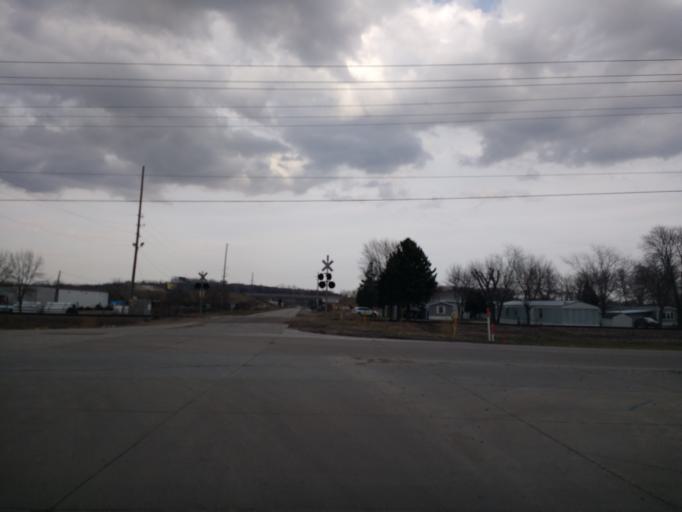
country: US
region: Iowa
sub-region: Woodbury County
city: Sergeant Bluff
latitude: 42.4074
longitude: -96.3703
